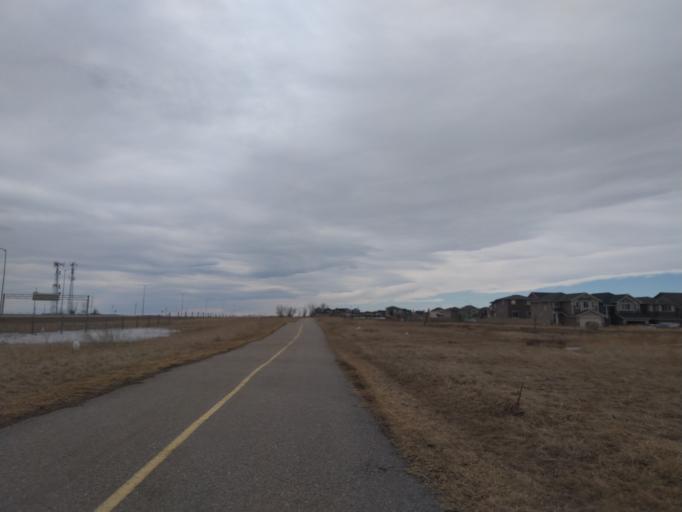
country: CA
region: Alberta
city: Chestermere
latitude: 51.1299
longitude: -113.9227
